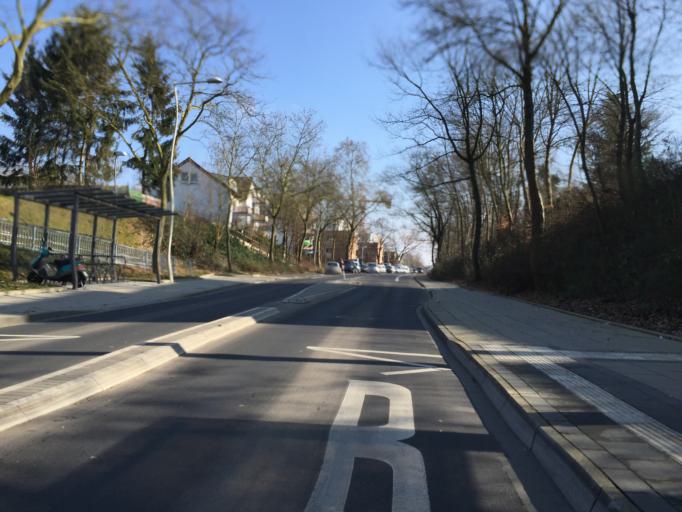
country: DE
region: North Rhine-Westphalia
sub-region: Regierungsbezirk Koln
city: Bonn
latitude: 50.7349
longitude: 7.0619
